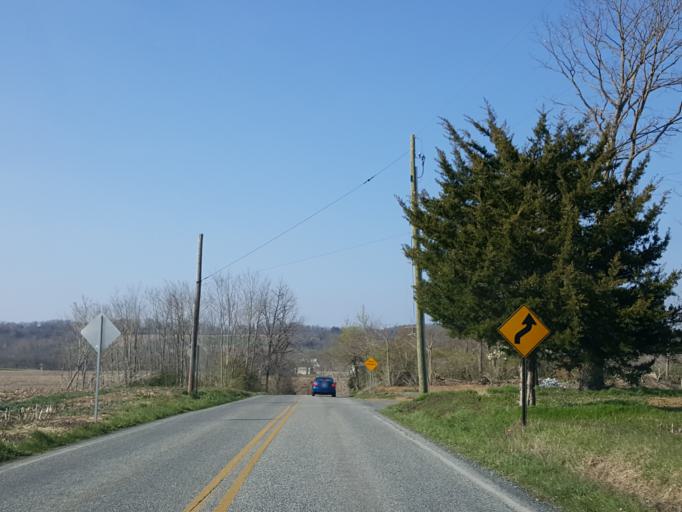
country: US
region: Pennsylvania
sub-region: Lebanon County
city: Annville
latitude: 40.3216
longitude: -76.5269
